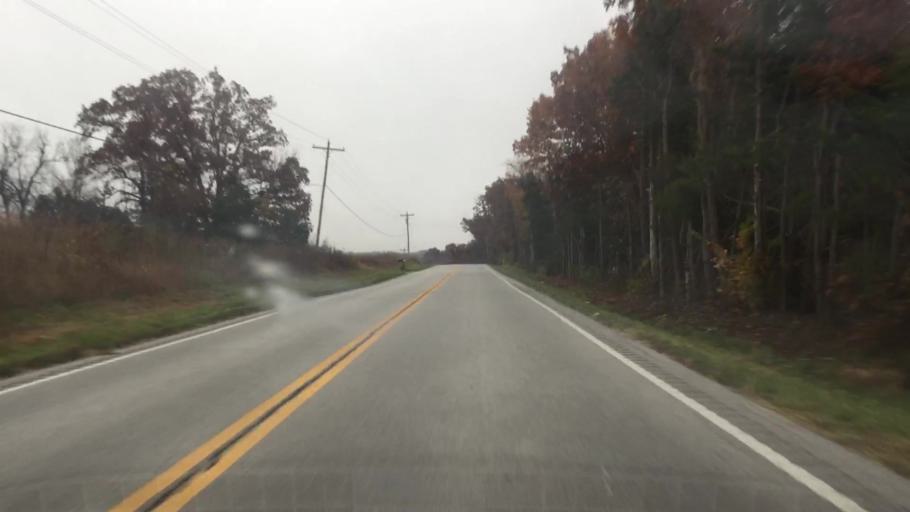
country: US
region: Missouri
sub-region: Callaway County
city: Fulton
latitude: 38.8853
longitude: -92.0951
